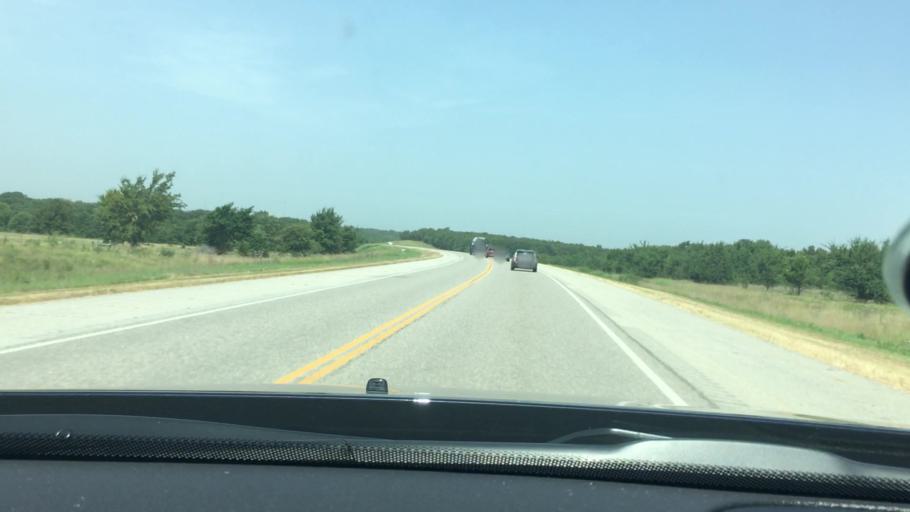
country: US
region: Oklahoma
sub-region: Coal County
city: Coalgate
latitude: 34.6094
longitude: -96.3817
